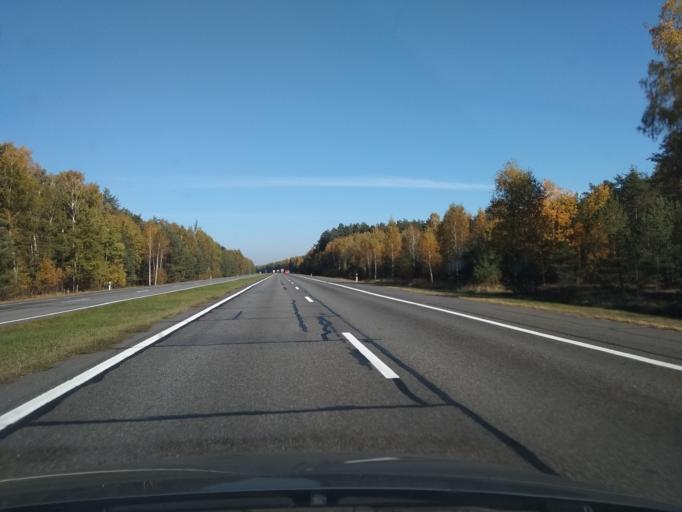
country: BY
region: Brest
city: Ivatsevichy
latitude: 52.7649
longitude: 25.5276
